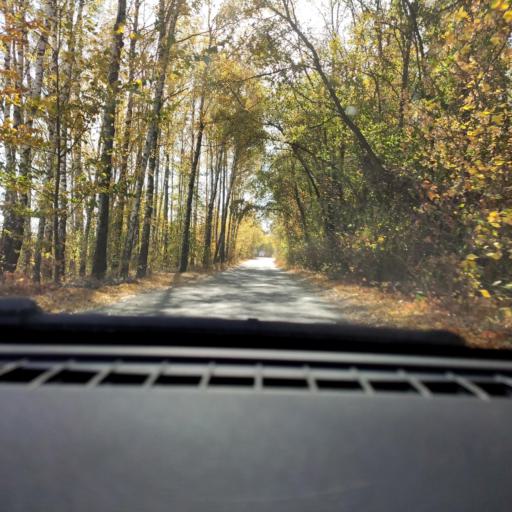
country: RU
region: Voronezj
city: Somovo
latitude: 51.6849
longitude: 39.2993
